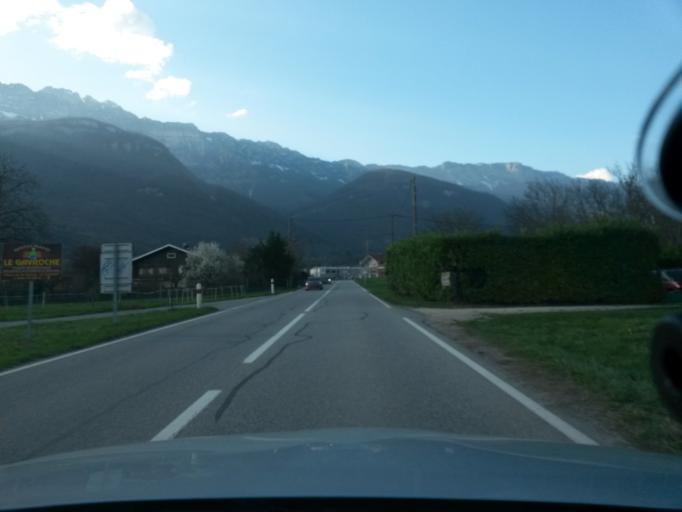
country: FR
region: Rhone-Alpes
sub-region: Departement de l'Isere
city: Le Touvet
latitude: 45.3558
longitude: 5.9580
